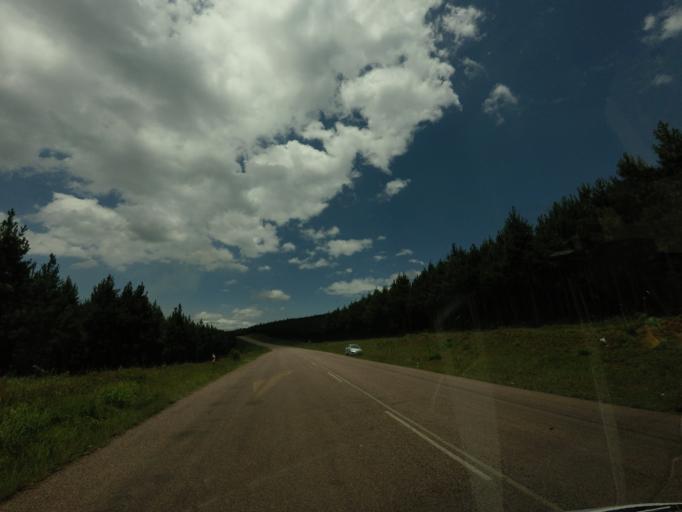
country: ZA
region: Mpumalanga
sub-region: Ehlanzeni District
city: Graksop
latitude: -25.0686
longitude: 30.8067
